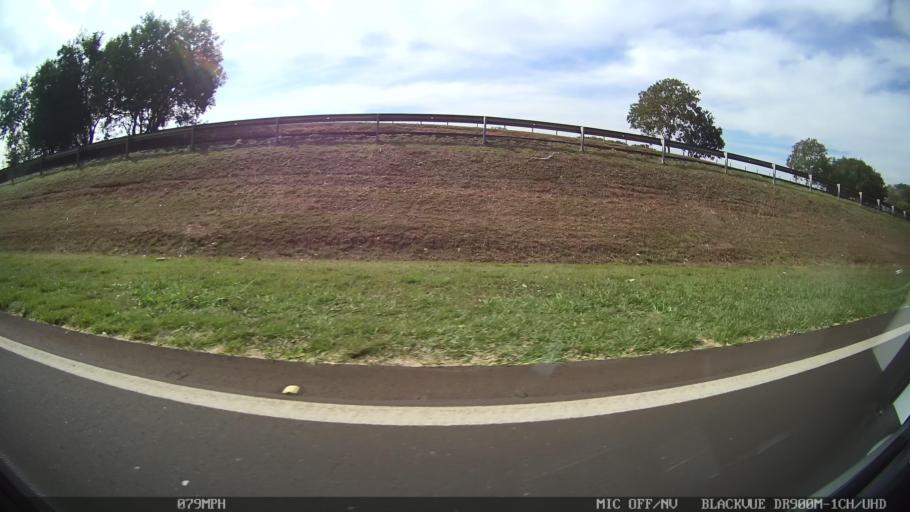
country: BR
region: Sao Paulo
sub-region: Matao
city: Matao
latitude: -21.6053
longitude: -48.4285
